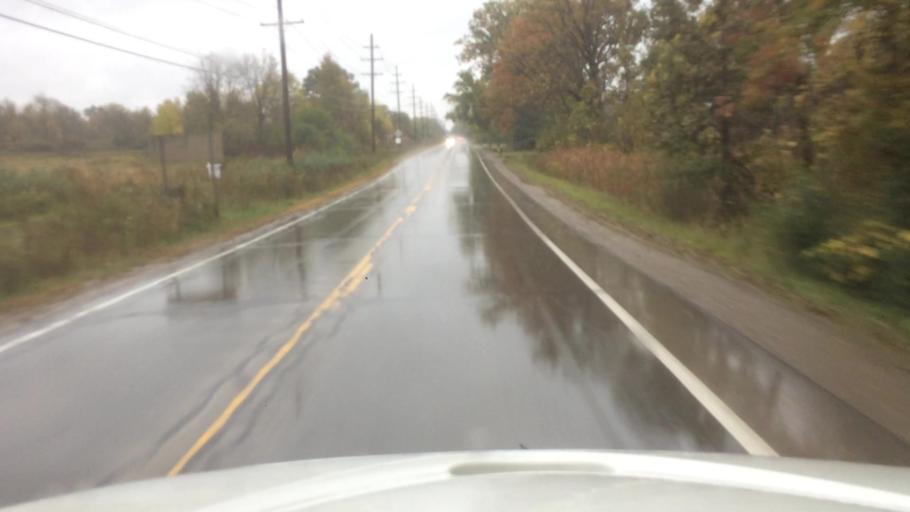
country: US
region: Michigan
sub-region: Oakland County
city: Oxford
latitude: 42.7825
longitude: -83.3197
